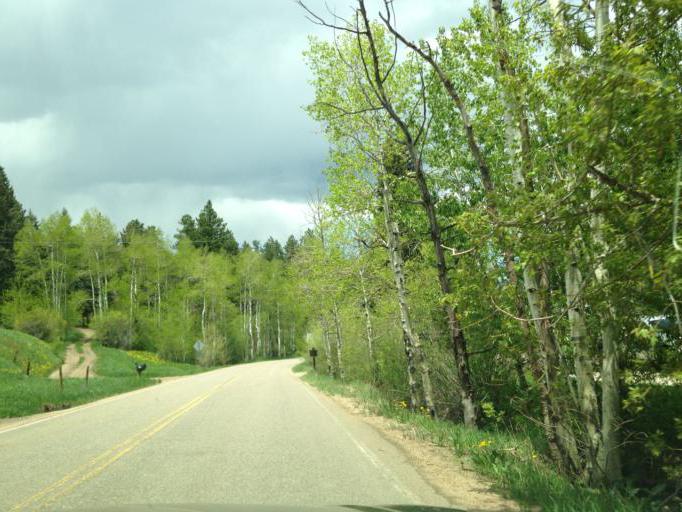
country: US
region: Colorado
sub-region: Jefferson County
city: Ken Caryl
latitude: 39.5128
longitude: -105.1859
